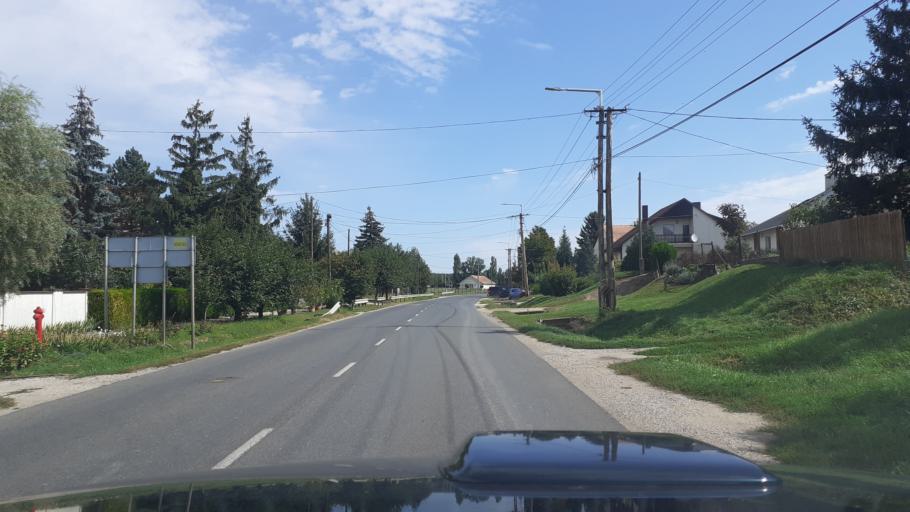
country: HU
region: Fejer
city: Seregelyes
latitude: 47.1106
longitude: 18.5865
